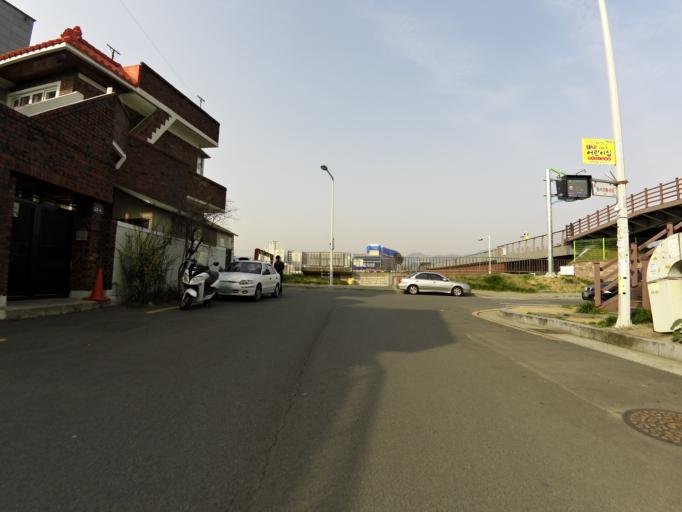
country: KR
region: Daegu
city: Daegu
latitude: 35.8891
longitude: 128.6371
